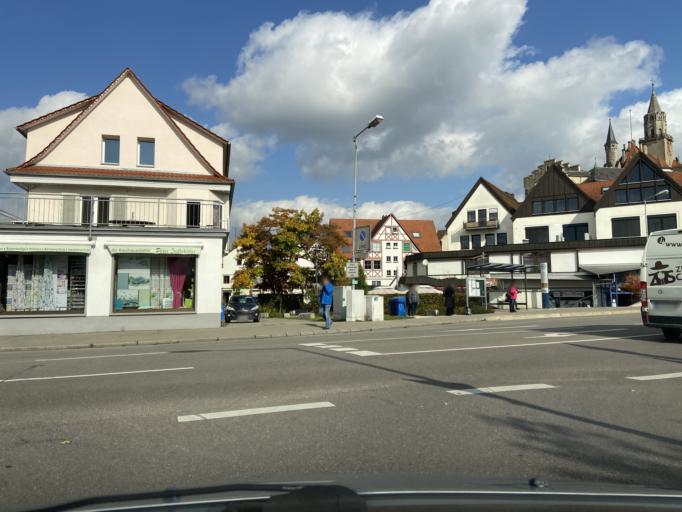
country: DE
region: Baden-Wuerttemberg
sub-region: Tuebingen Region
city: Sigmaringen
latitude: 48.0865
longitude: 9.2136
